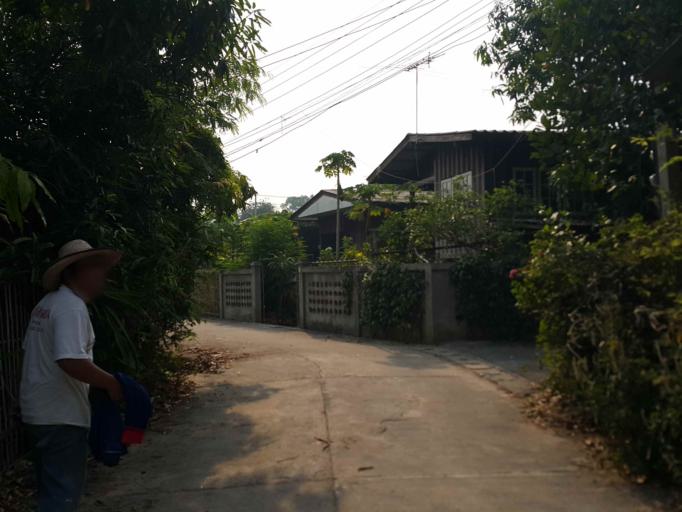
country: TH
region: Chiang Mai
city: San Kamphaeng
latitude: 18.7932
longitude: 99.0845
